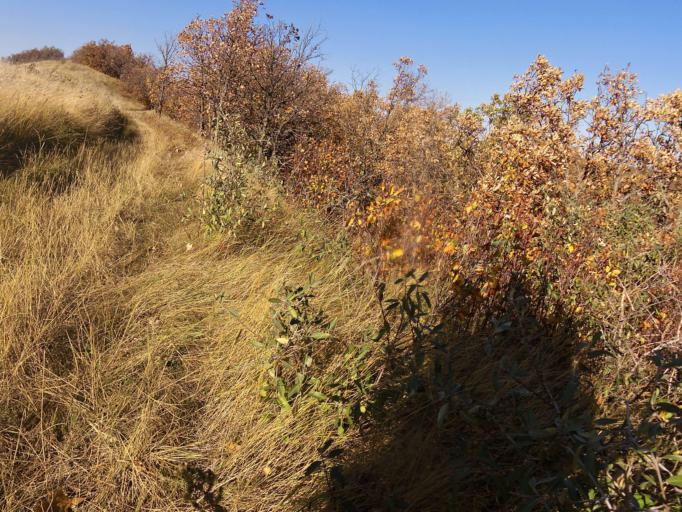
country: CA
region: Manitoba
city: Morden
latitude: 48.9453
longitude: -98.0735
